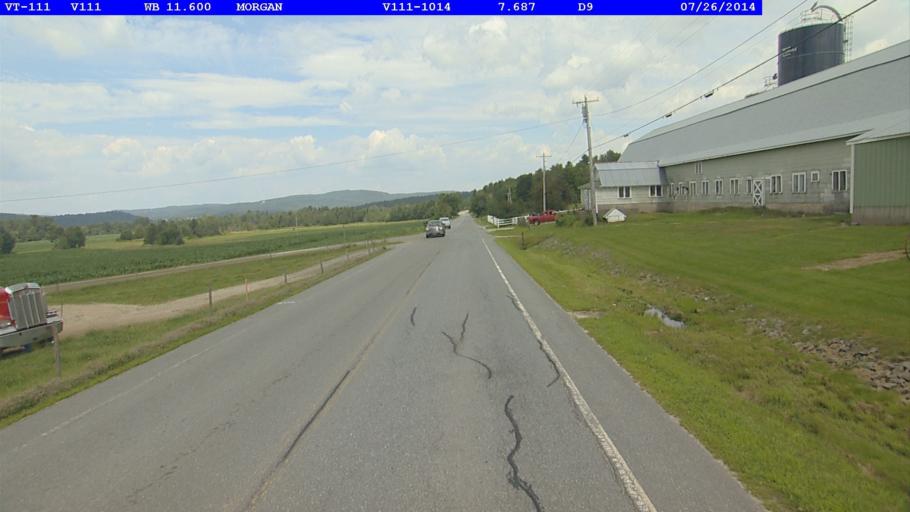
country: US
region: Vermont
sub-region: Orleans County
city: Newport
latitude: 44.8733
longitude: -71.9586
